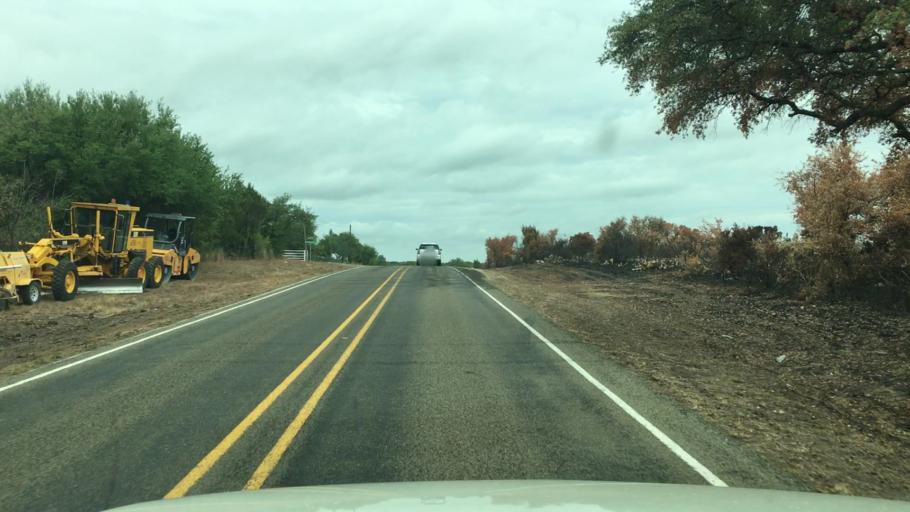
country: US
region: Texas
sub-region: Llano County
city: Horseshoe Bay
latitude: 30.4818
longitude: -98.4249
